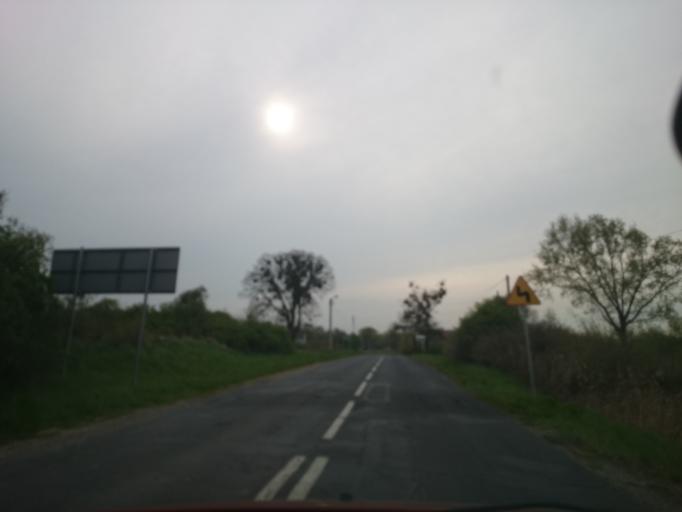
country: PL
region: Opole Voivodeship
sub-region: Powiat nyski
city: Sidzina
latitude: 50.6431
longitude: 17.4905
